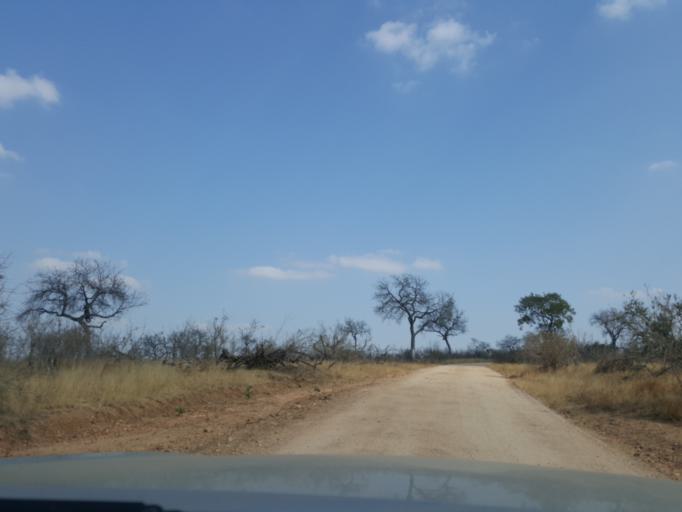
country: ZA
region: Mpumalanga
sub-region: Ehlanzeni District
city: Komatipoort
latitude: -25.2924
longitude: 31.7635
